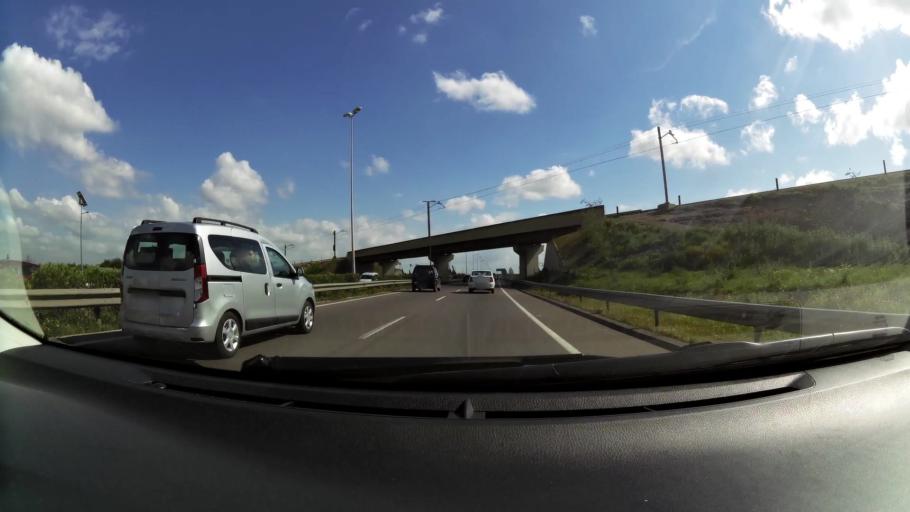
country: MA
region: Chaouia-Ouardigha
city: Nouaseur
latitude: 33.3975
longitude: -7.6208
